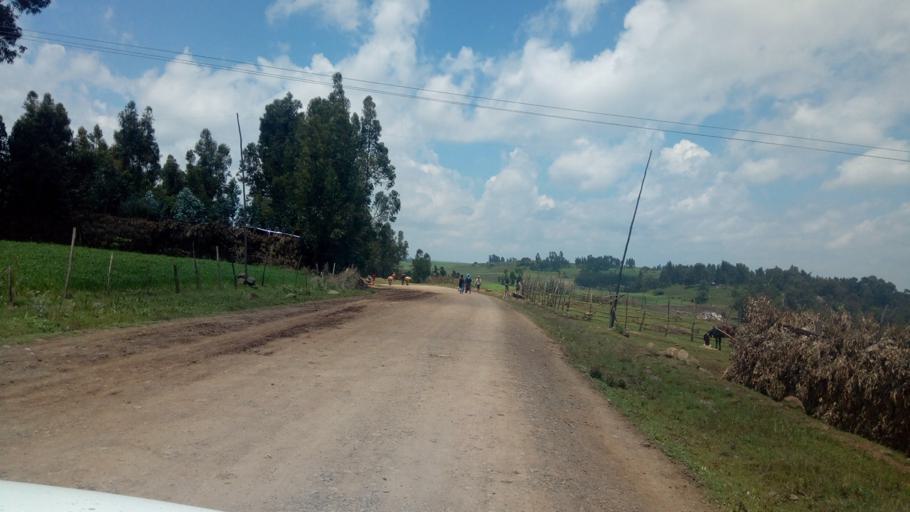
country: ET
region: Oromiya
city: Sendafa
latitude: 8.9770
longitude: 39.1228
